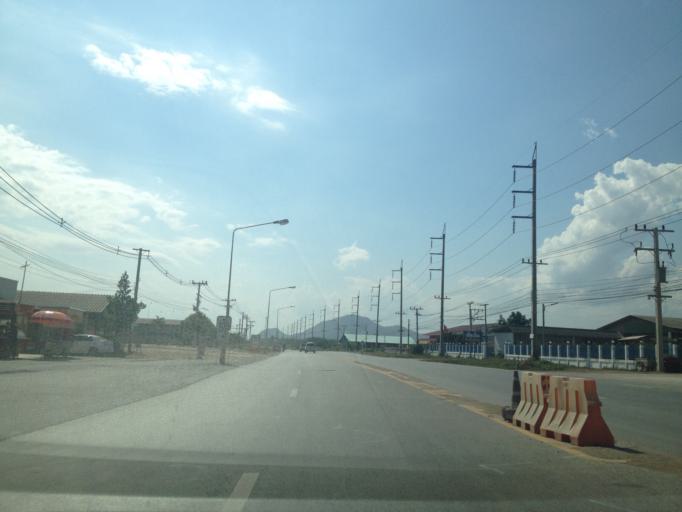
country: TH
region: Chiang Mai
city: Hot
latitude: 18.2898
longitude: 98.6408
